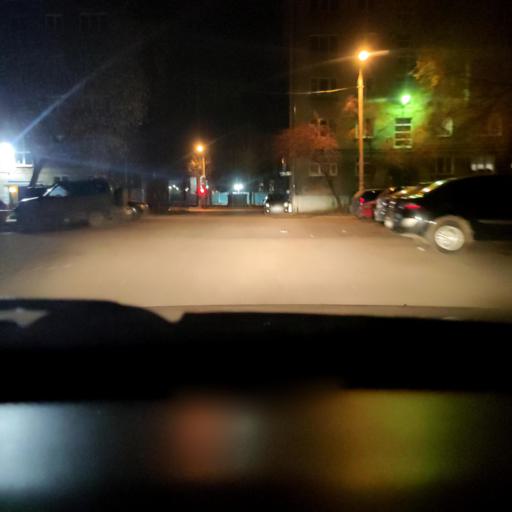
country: RU
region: Perm
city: Froly
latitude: 57.9572
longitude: 56.2413
